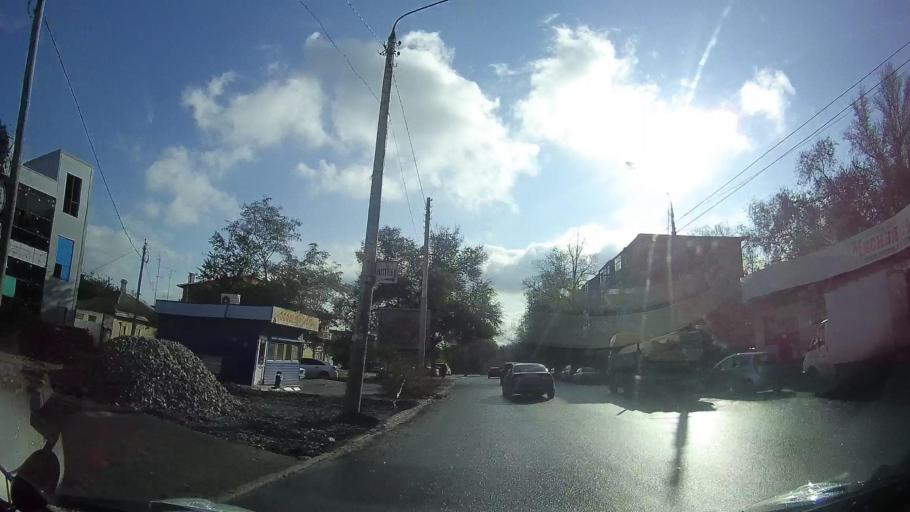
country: RU
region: Rostov
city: Severnyy
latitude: 47.2628
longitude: 39.6696
